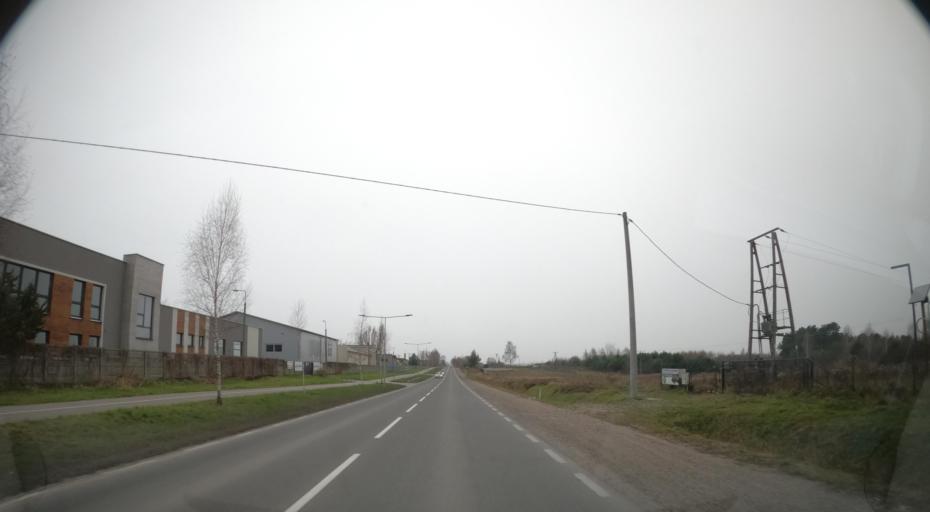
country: PL
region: Masovian Voivodeship
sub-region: Radom
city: Radom
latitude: 51.4438
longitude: 21.1907
